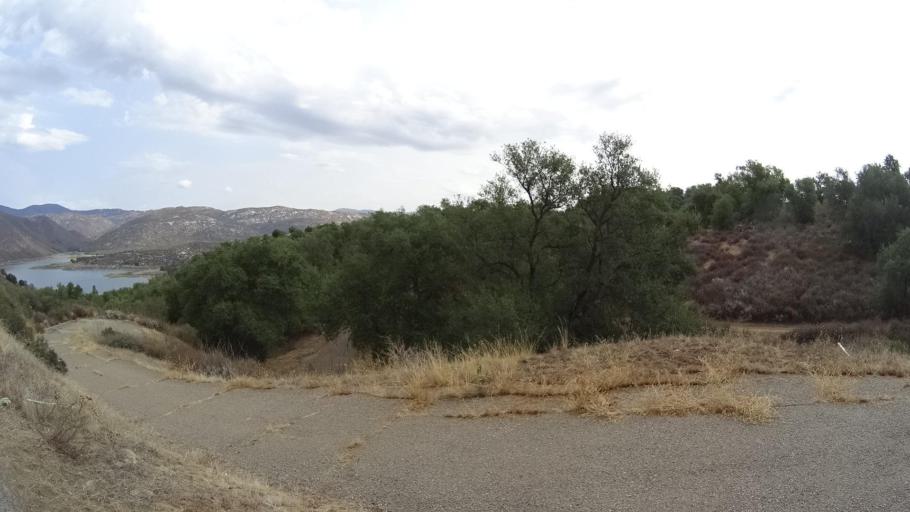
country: US
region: California
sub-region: San Diego County
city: San Diego Country Estates
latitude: 33.0982
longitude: -116.7894
